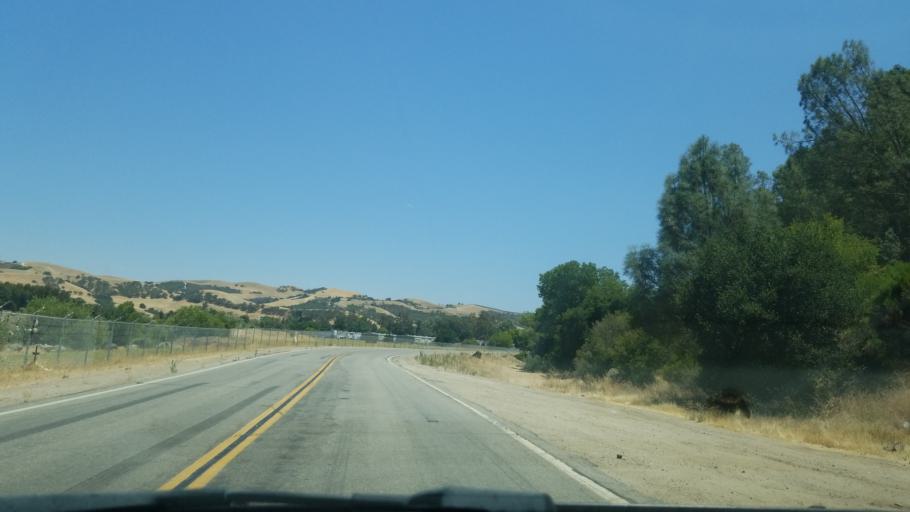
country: US
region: California
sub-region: San Luis Obispo County
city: Atascadero
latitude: 35.4989
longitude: -120.6574
